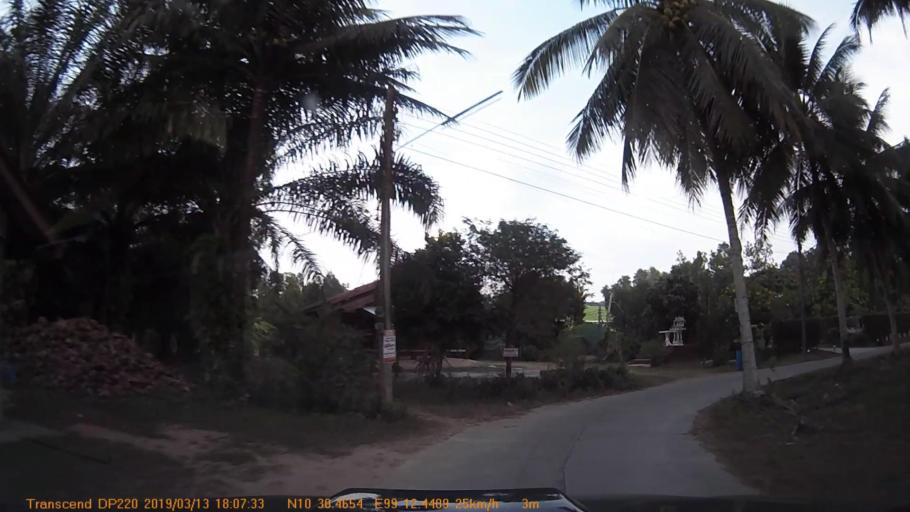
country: TH
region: Chumphon
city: Chumphon
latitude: 10.5076
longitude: 99.2075
